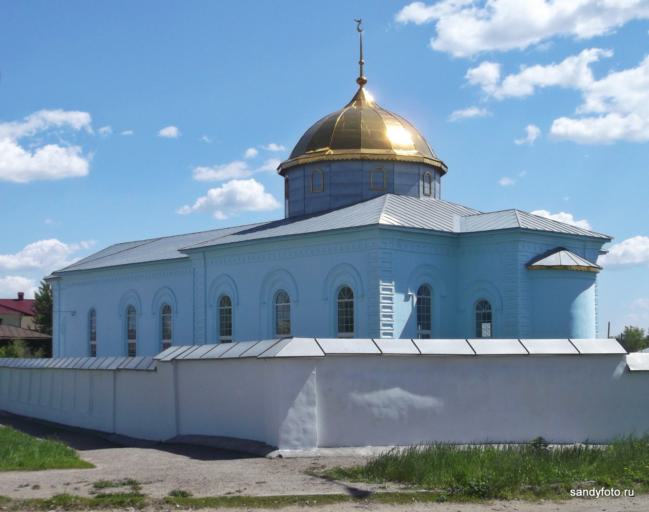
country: RU
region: Chelyabinsk
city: Troitsk
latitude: 54.0835
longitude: 61.5682
